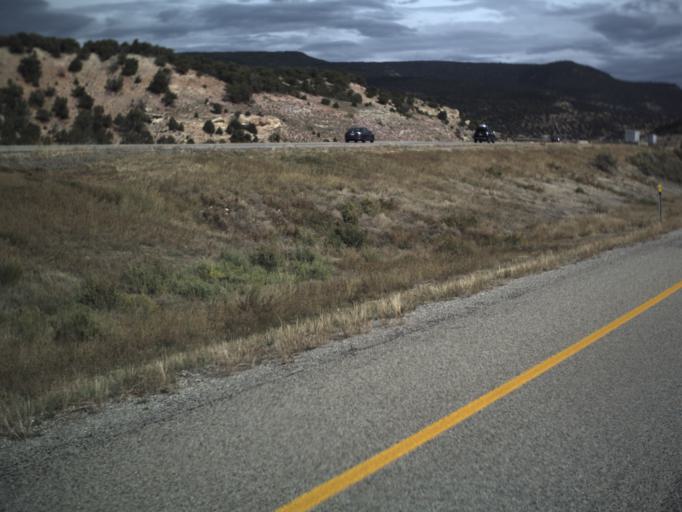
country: US
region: Utah
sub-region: Sevier County
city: Salina
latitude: 38.9166
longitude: -111.7438
